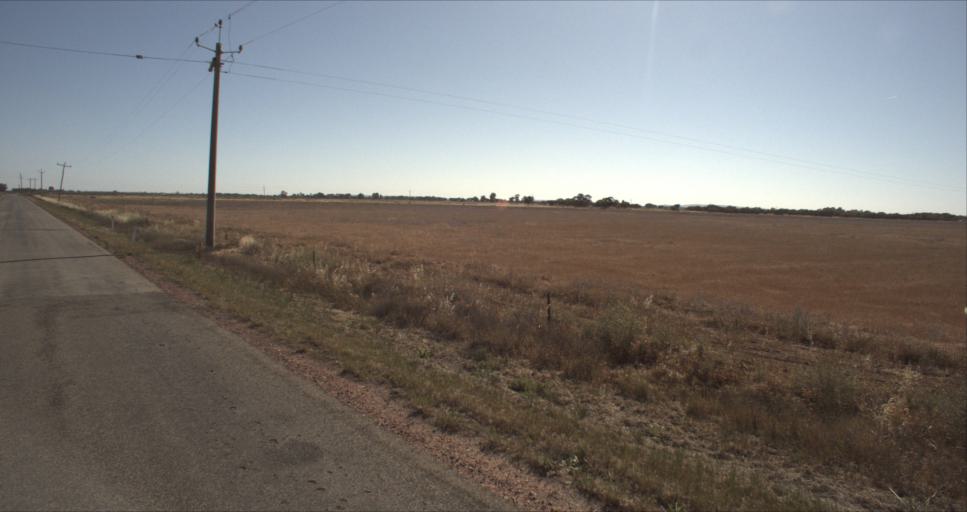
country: AU
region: New South Wales
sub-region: Leeton
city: Leeton
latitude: -34.5538
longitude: 146.2668
